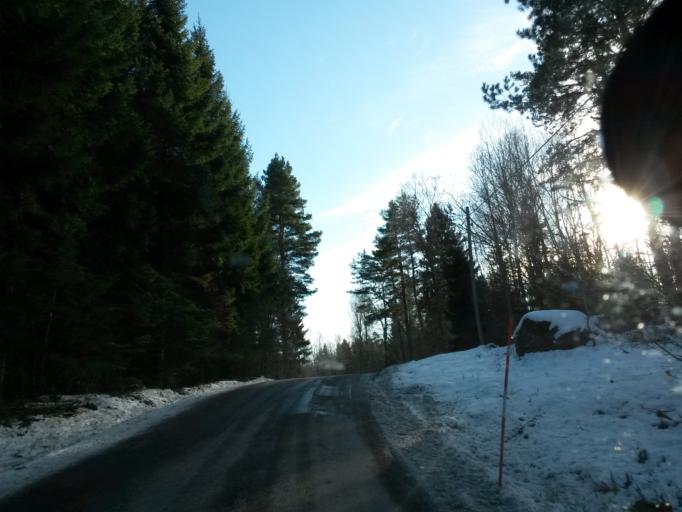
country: SE
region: Vaestra Goetaland
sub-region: Vargarda Kommun
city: Vargarda
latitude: 58.0199
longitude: 12.8898
